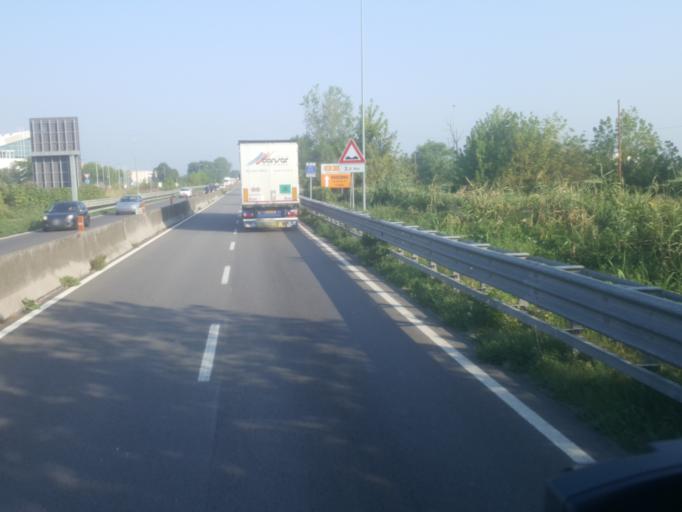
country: IT
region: Emilia-Romagna
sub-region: Provincia di Ravenna
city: Ravenna
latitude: 44.4129
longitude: 12.1711
